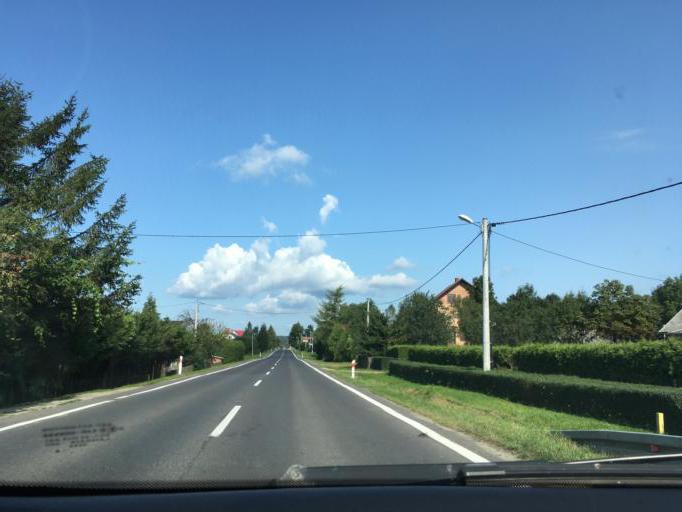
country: PL
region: Subcarpathian Voivodeship
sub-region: Powiat leski
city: Olszanica
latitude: 49.4638
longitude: 22.4699
